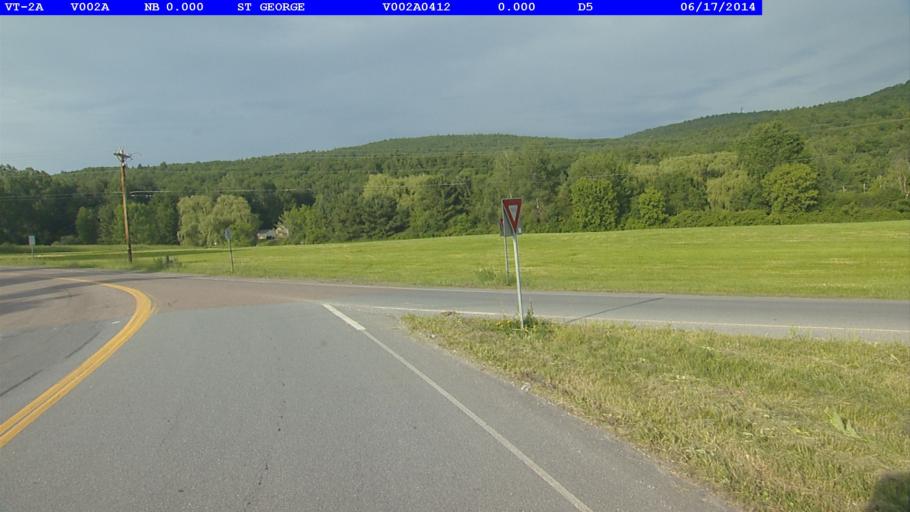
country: US
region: Vermont
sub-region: Chittenden County
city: Hinesburg
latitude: 44.3698
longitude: -73.1283
